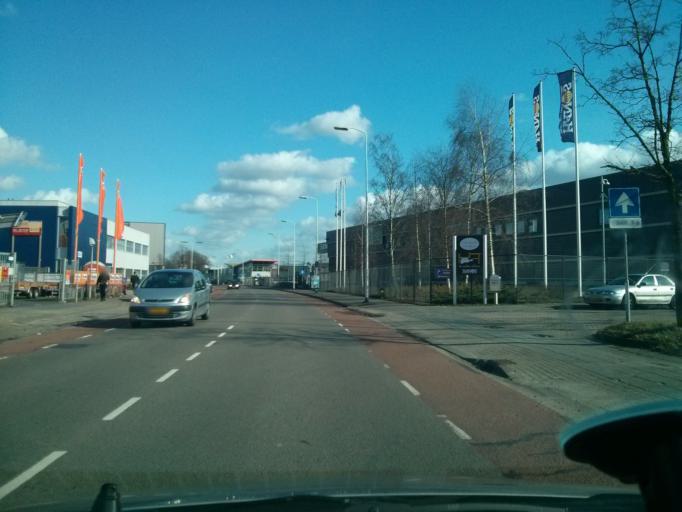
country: NL
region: North Brabant
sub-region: Gemeente Eindhoven
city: Meerhoven
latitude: 51.4346
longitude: 5.4311
